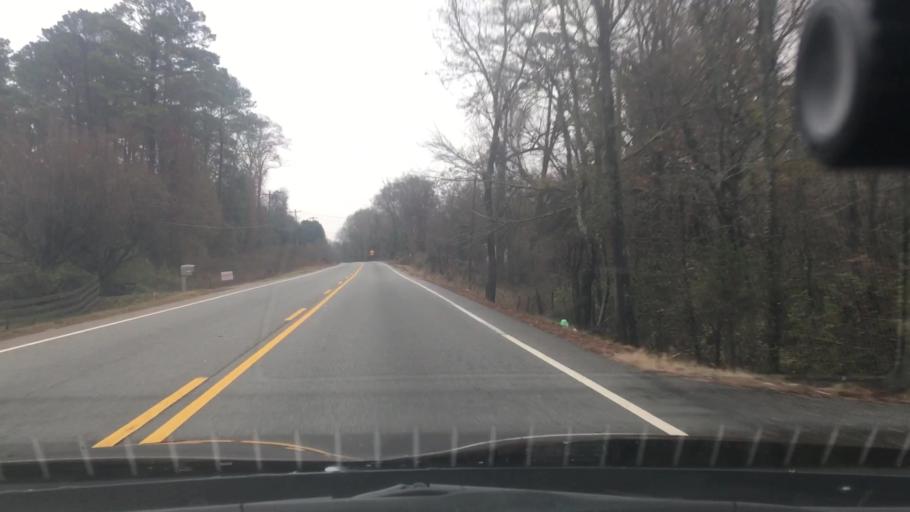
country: US
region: Georgia
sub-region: Spalding County
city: Experiment
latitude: 33.2396
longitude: -84.3332
